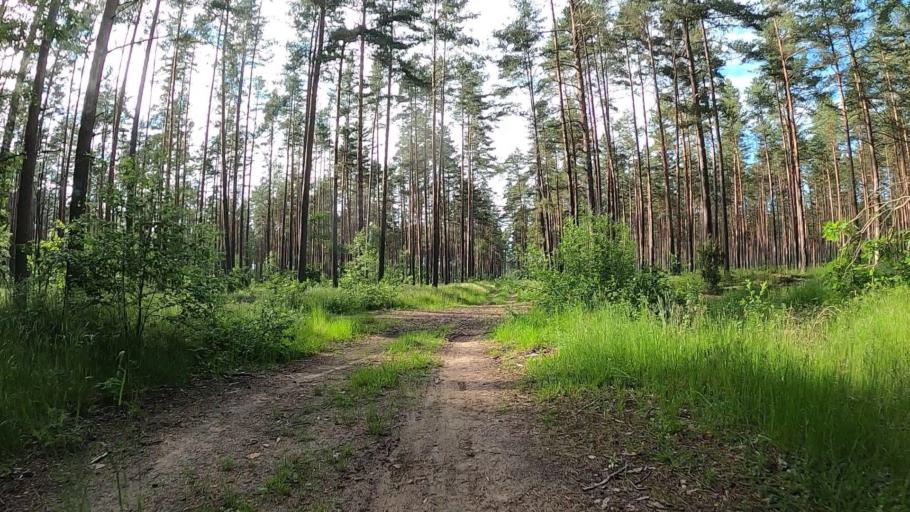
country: LV
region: Riga
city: Bergi
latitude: 57.0161
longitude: 24.2421
